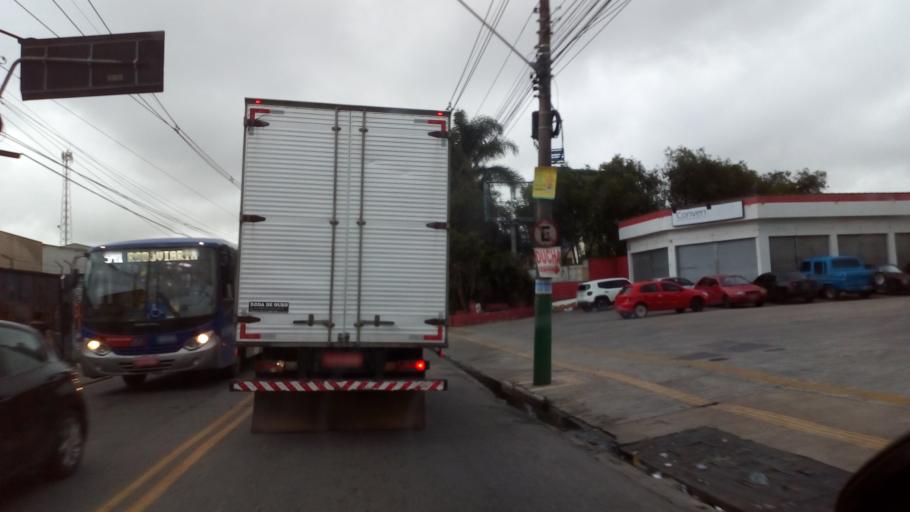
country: BR
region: Sao Paulo
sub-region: Itaquaquecetuba
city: Itaquaquecetuba
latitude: -23.4407
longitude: -46.4076
